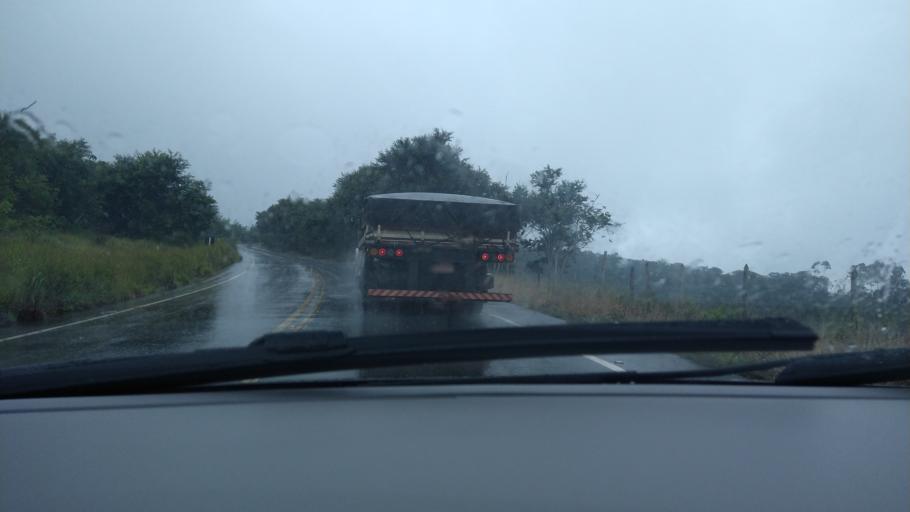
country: BR
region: Minas Gerais
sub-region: Ponte Nova
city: Ponte Nova
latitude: -20.5757
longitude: -42.8762
